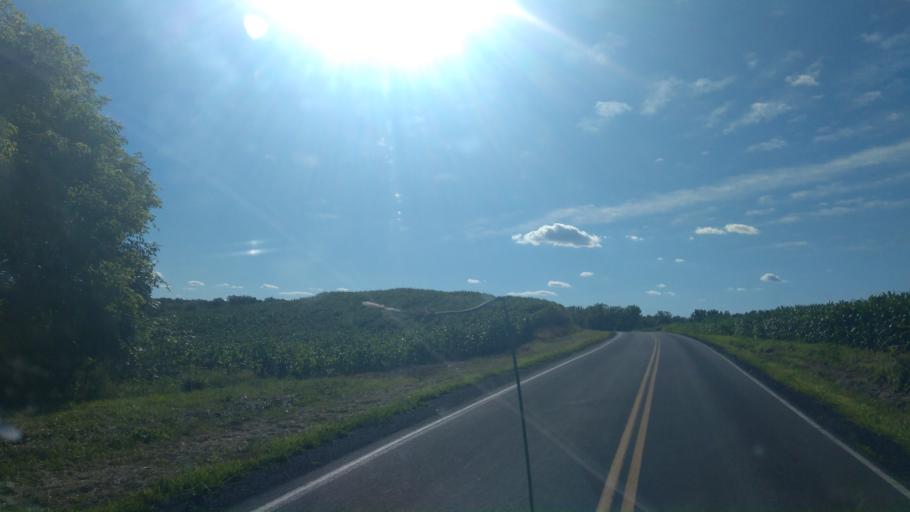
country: US
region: New York
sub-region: Wayne County
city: Lyons
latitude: 42.9971
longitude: -76.9435
